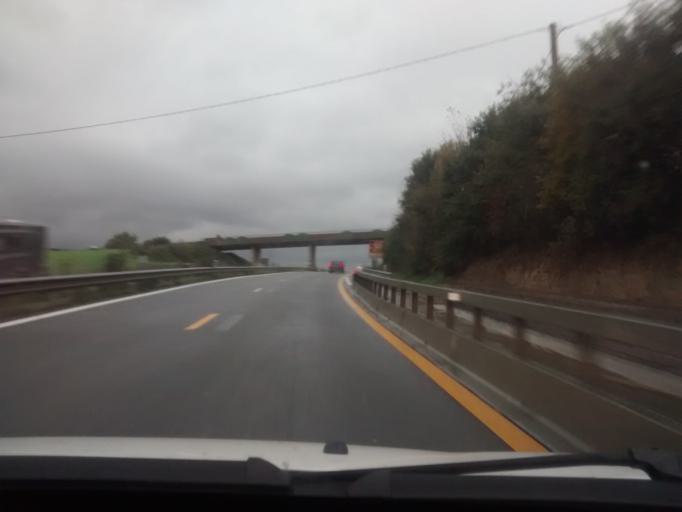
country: FR
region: Brittany
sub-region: Departement d'Ille-et-Vilaine
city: Saint-Pere
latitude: 48.5530
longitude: -1.9264
